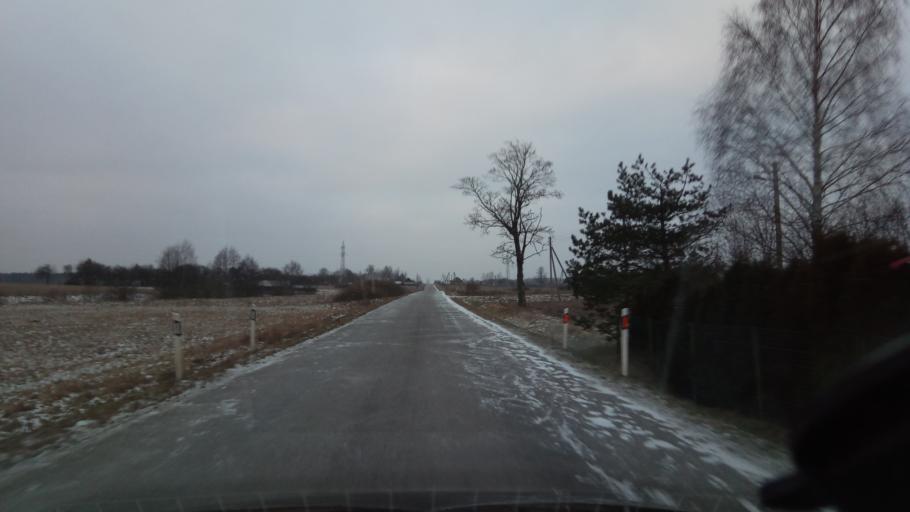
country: LT
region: Alytaus apskritis
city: Varena
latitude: 54.1169
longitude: 24.7520
